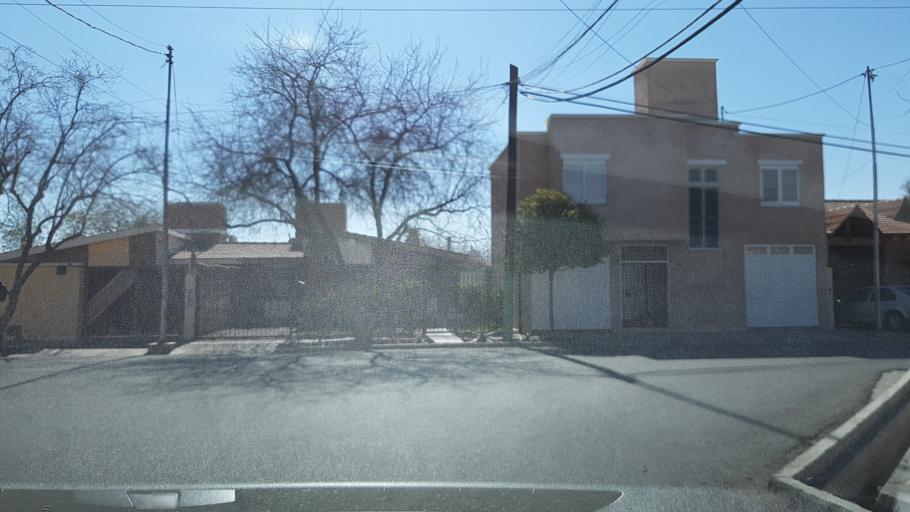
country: AR
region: San Juan
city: San Juan
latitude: -31.5372
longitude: -68.5819
